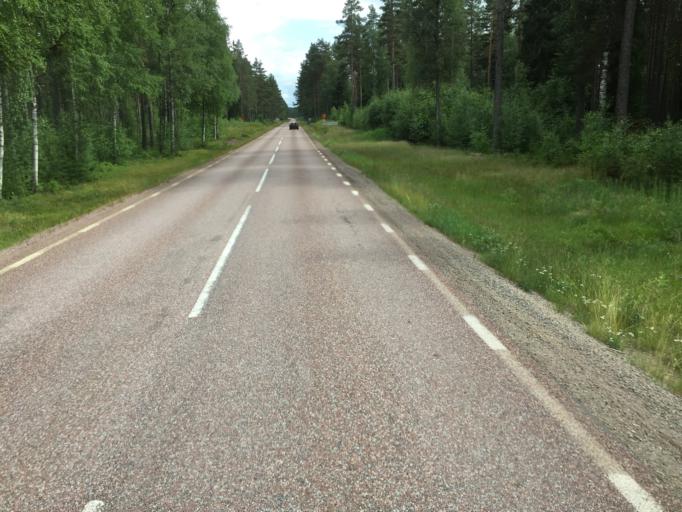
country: SE
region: Dalarna
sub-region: Vansbro Kommun
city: Vansbro
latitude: 60.8237
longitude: 14.1270
